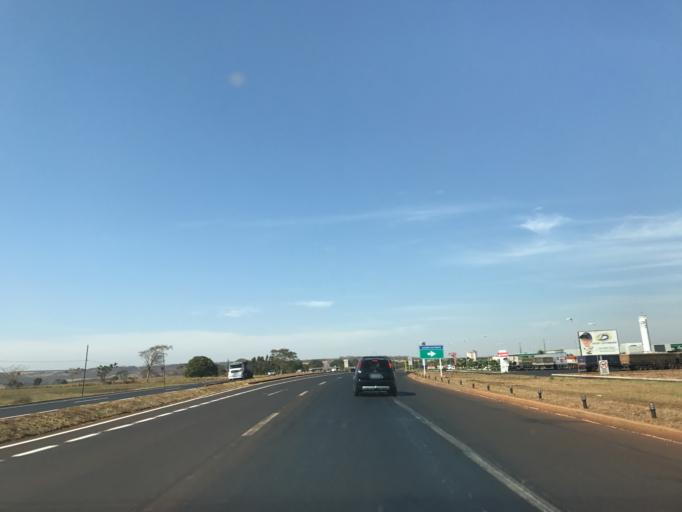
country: BR
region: Minas Gerais
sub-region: Centralina
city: Centralina
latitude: -18.5726
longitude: -49.1938
